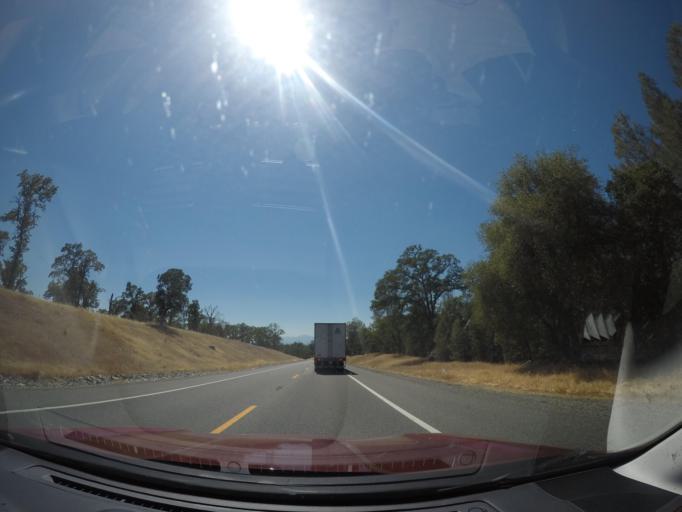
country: US
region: California
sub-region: Shasta County
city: Bella Vista
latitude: 40.6874
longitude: -122.1347
